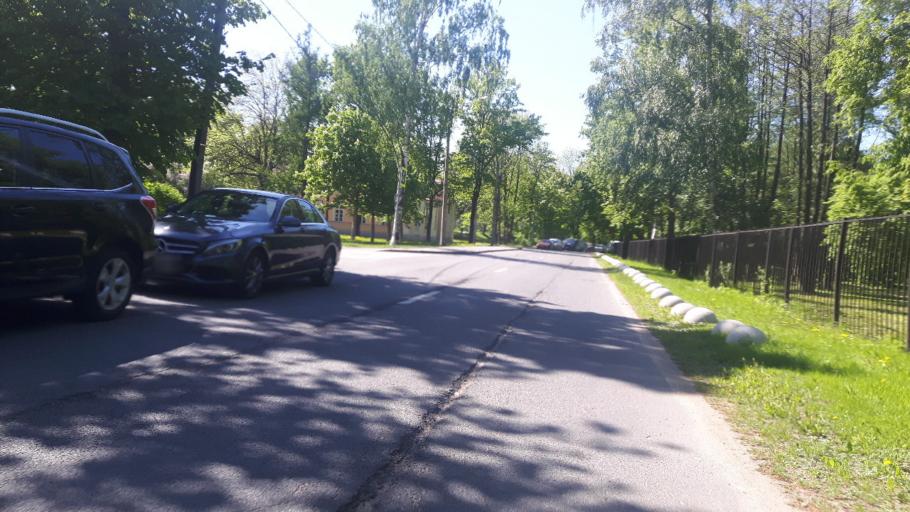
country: RU
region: St.-Petersburg
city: Peterhof
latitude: 59.8811
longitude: 29.9226
